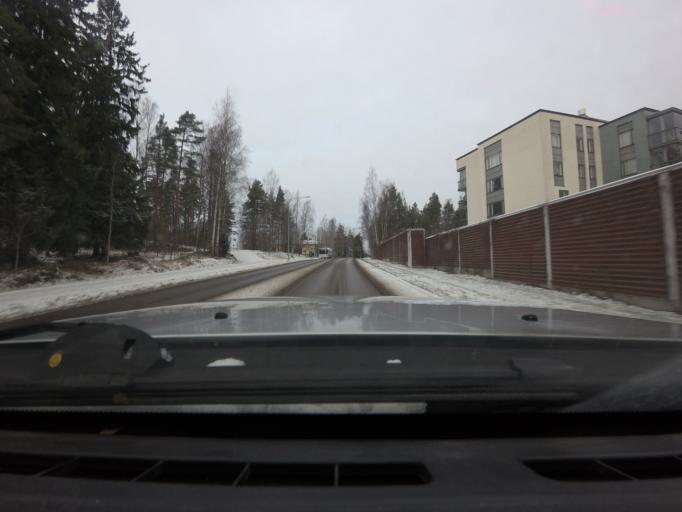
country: FI
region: Uusimaa
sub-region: Helsinki
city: Kilo
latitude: 60.2321
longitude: 24.7743
